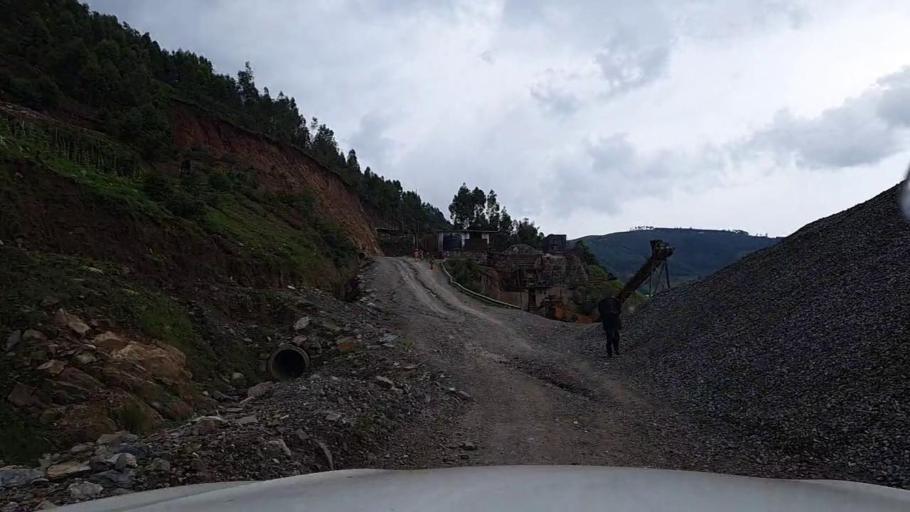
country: RW
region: Northern Province
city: Byumba
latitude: -1.6265
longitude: 29.9229
